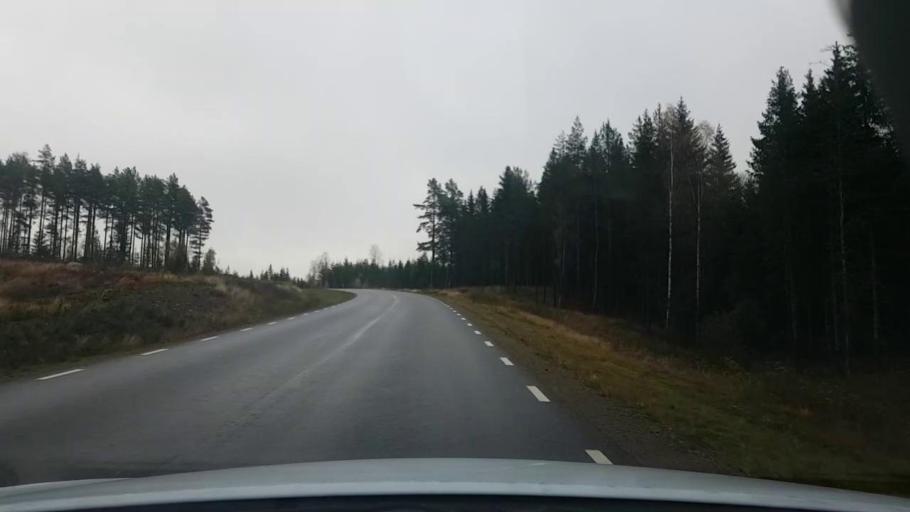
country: SE
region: Vaestra Goetaland
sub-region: Karlsborgs Kommun
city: Karlsborg
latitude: 58.6832
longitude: 14.4952
